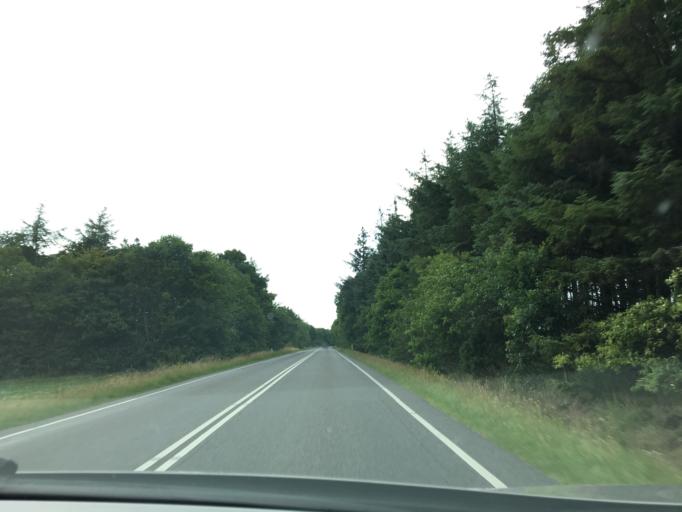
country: DK
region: South Denmark
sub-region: Varde Kommune
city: Oksbol
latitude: 55.7032
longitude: 8.3137
